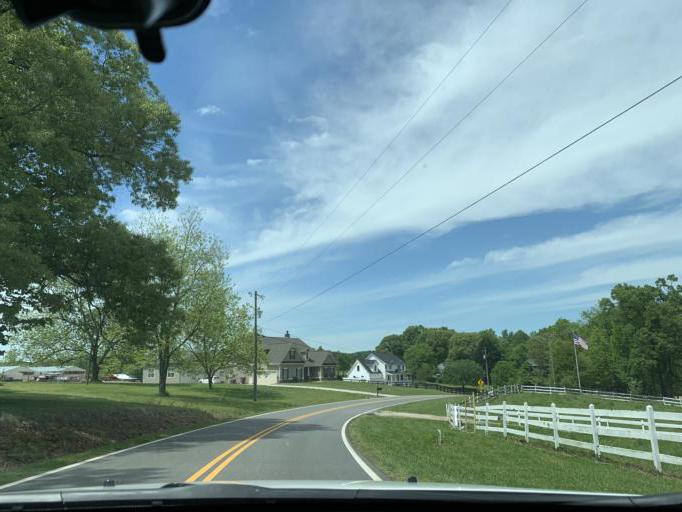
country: US
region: Georgia
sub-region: Hall County
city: Flowery Branch
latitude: 34.2687
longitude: -84.0238
